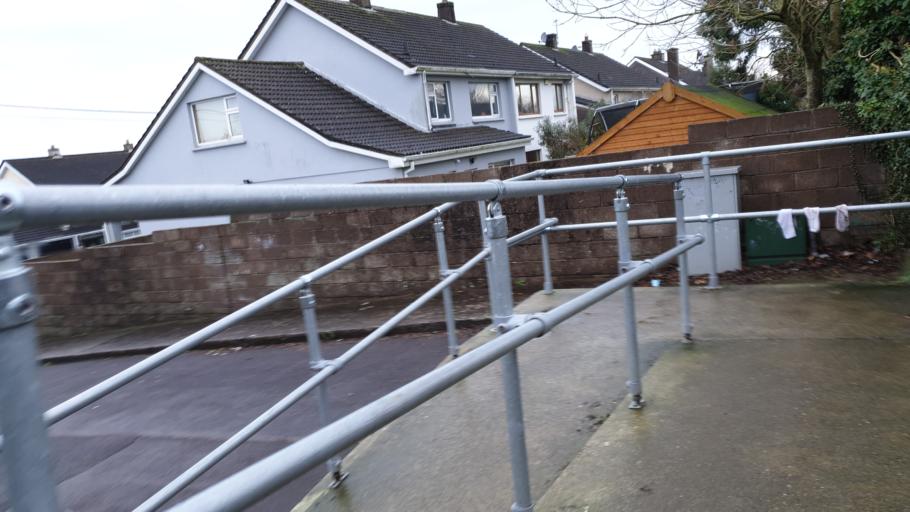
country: IE
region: Munster
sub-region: County Cork
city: Cork
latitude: 51.8884
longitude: -8.4307
